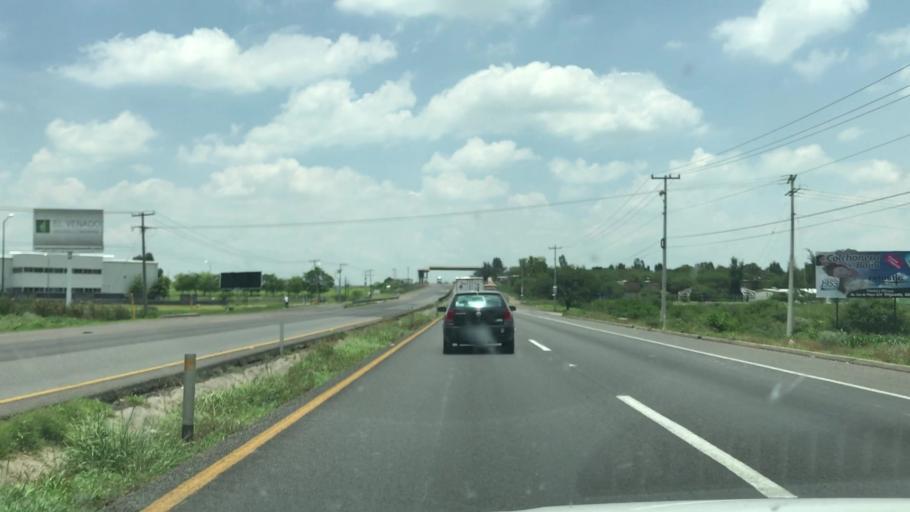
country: MX
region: Guanajuato
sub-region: Irapuato
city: Colonia Morelos de Guadalupe de Rivera
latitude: 20.5782
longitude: -101.4364
